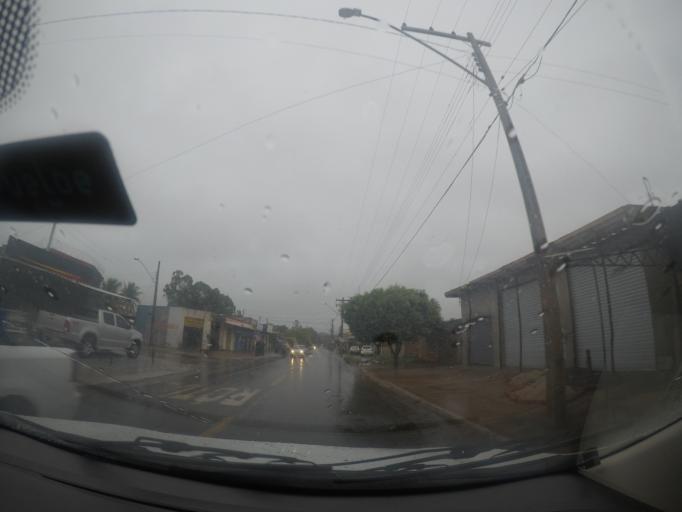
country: BR
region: Goias
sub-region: Goiania
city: Goiania
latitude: -16.6076
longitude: -49.3470
